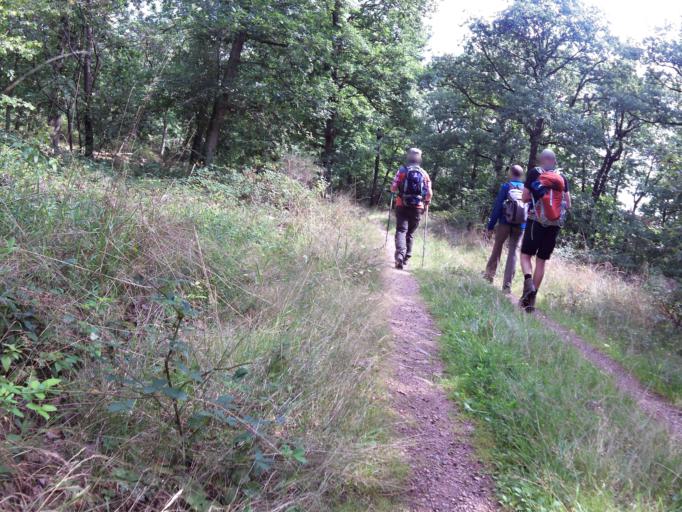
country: DE
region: Rheinland-Pfalz
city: Bad Munster am Stein-Ebernburg
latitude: 49.8275
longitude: 7.8401
